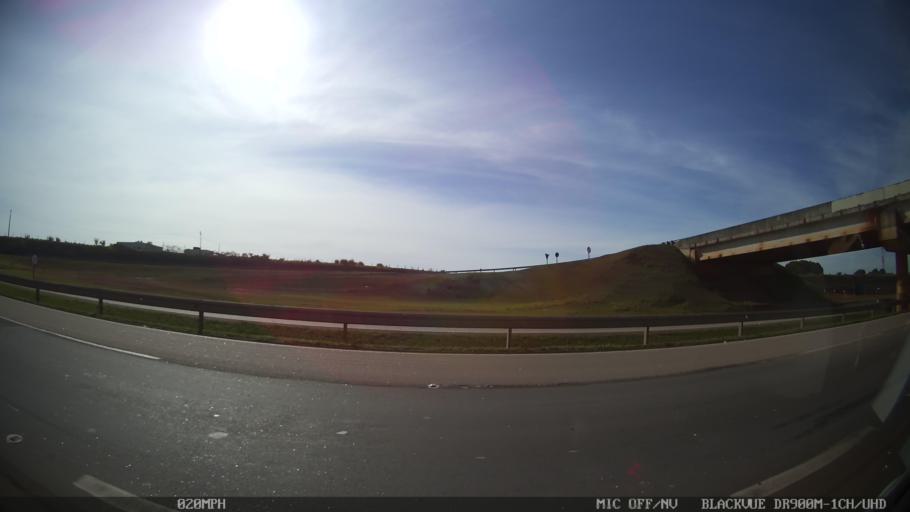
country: BR
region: Sao Paulo
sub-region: Rio Das Pedras
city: Rio das Pedras
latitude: -22.7821
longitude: -47.5877
